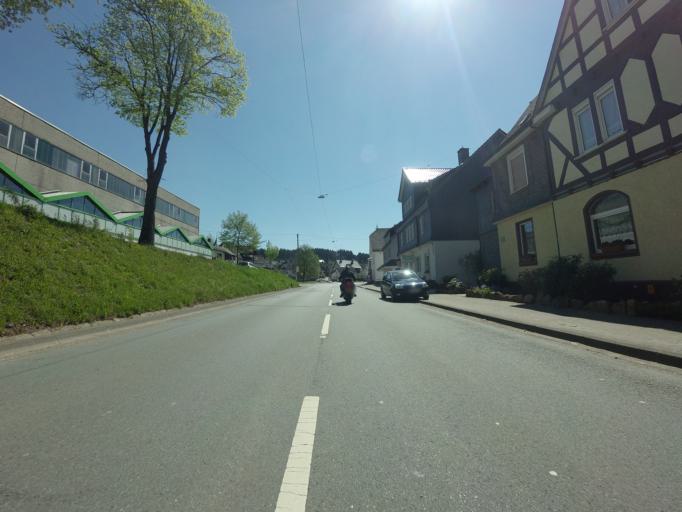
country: DE
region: North Rhine-Westphalia
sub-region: Regierungsbezirk Arnsberg
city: Kirchhundem
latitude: 51.0876
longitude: 8.1196
